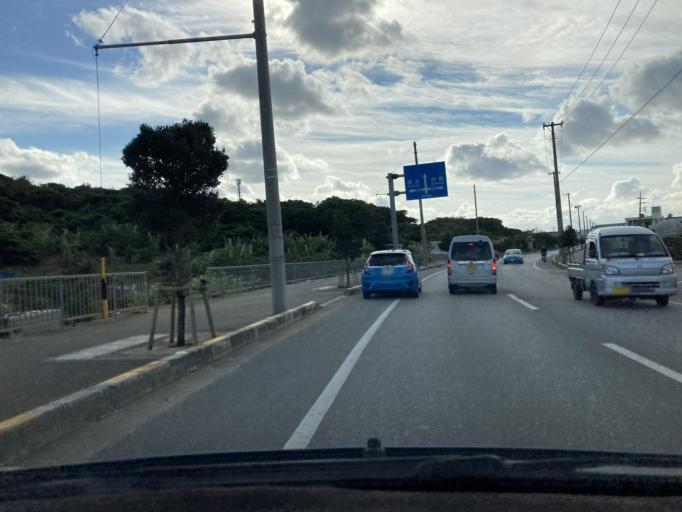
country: JP
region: Okinawa
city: Itoman
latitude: 26.1255
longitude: 127.6811
